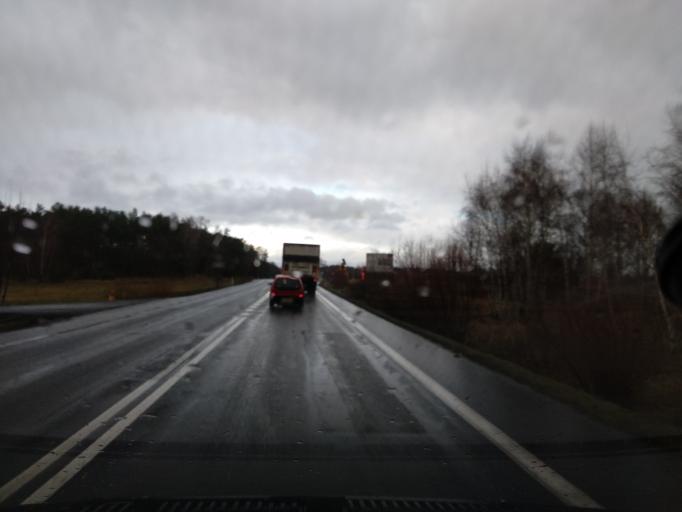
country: PL
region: Greater Poland Voivodeship
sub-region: Powiat koninski
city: Stare Miasto
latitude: 52.1683
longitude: 18.2106
